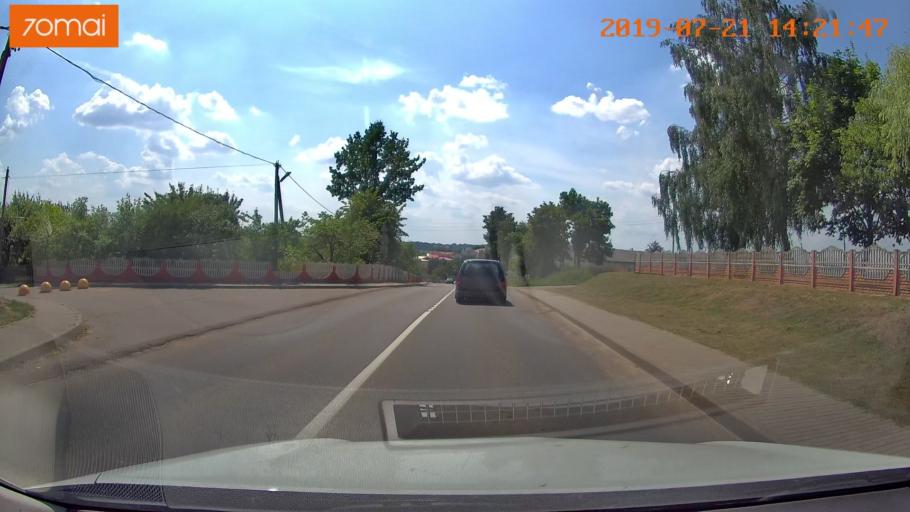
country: BY
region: Grodnenskaya
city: Karelichy
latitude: 53.5751
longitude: 26.1424
